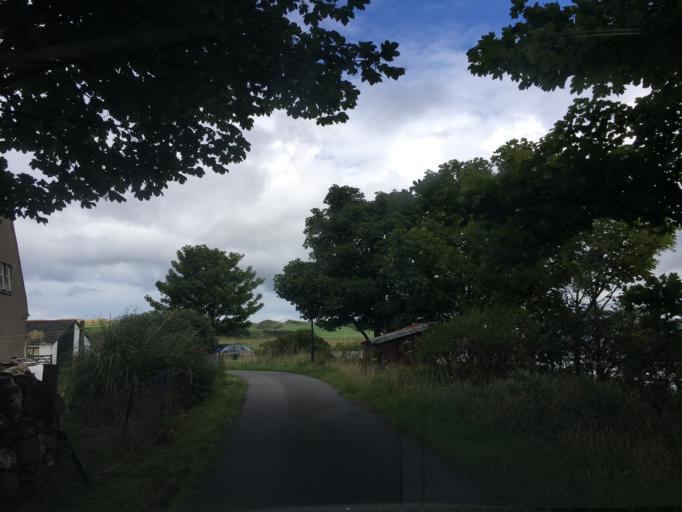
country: GB
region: Scotland
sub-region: Argyll and Bute
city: Oban
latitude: 56.2175
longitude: -5.6311
